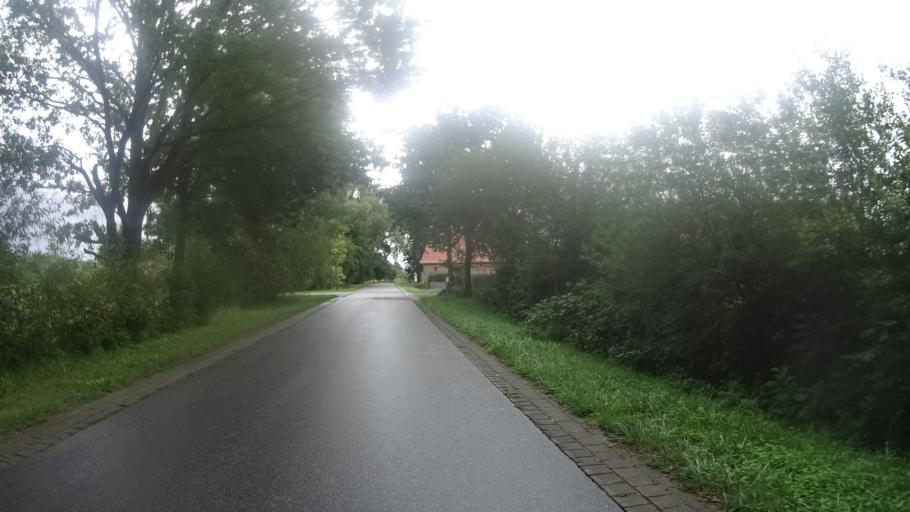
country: DE
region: Lower Saxony
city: Neu Darchau
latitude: 53.2496
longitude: 10.8807
